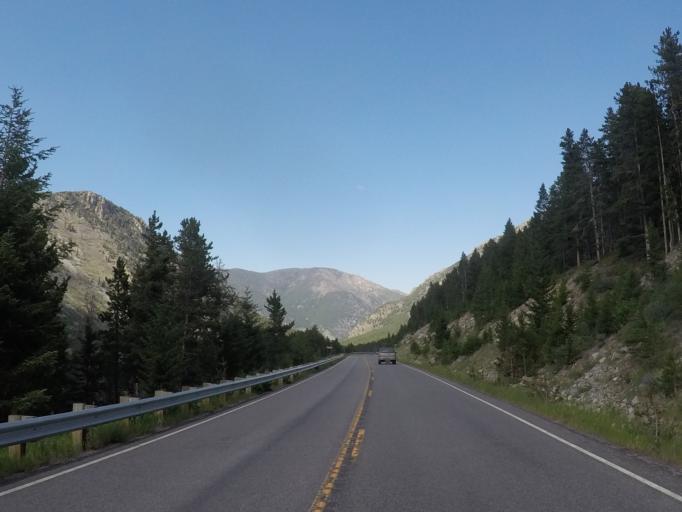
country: US
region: Montana
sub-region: Carbon County
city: Red Lodge
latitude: 45.0560
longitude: -109.4070
